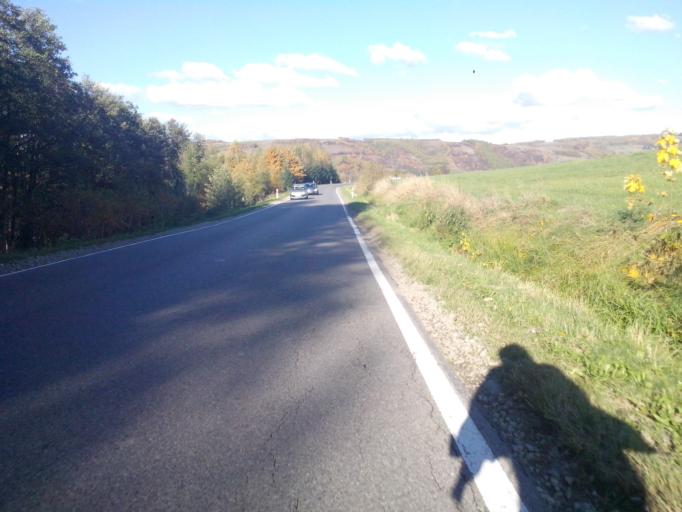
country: PL
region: Subcarpathian Voivodeship
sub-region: Powiat strzyzowski
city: Jawornik
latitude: 49.7996
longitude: 21.8634
